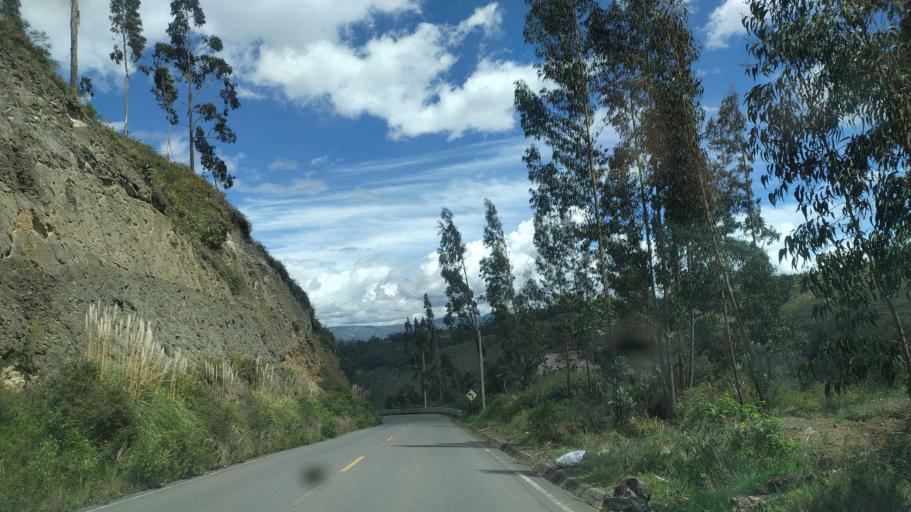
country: EC
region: Chimborazo
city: Riobamba
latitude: -1.6613
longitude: -78.5837
